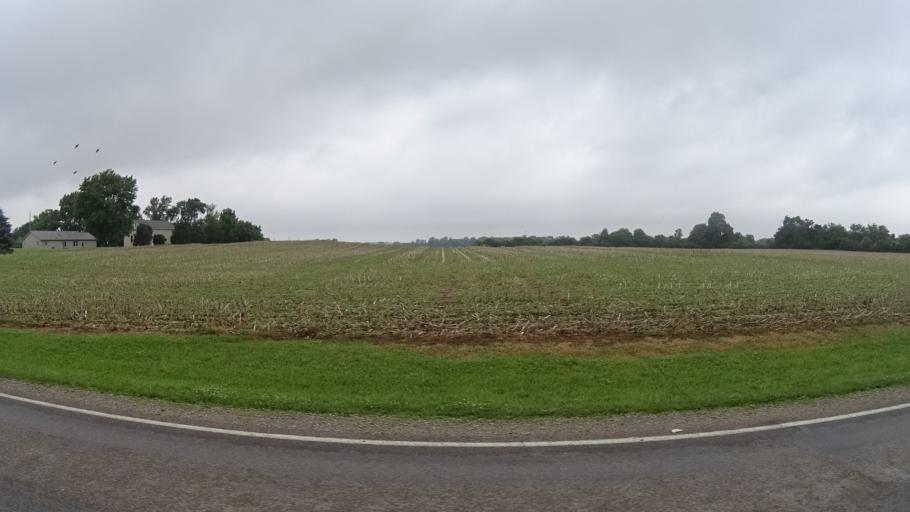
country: US
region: Ohio
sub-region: Huron County
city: Bellevue
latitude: 41.3422
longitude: -82.8286
